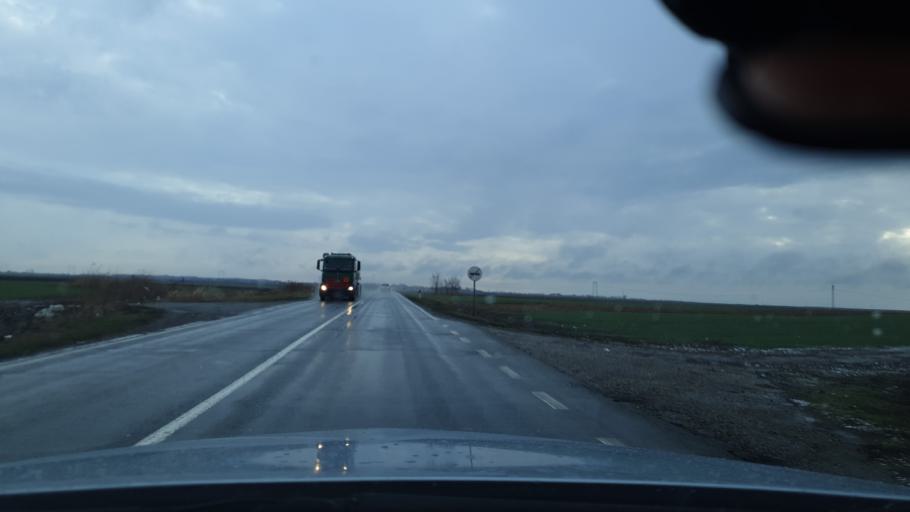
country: RS
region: Autonomna Pokrajina Vojvodina
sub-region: Juznobanatski Okrug
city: Kovin
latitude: 44.8304
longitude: 20.8332
